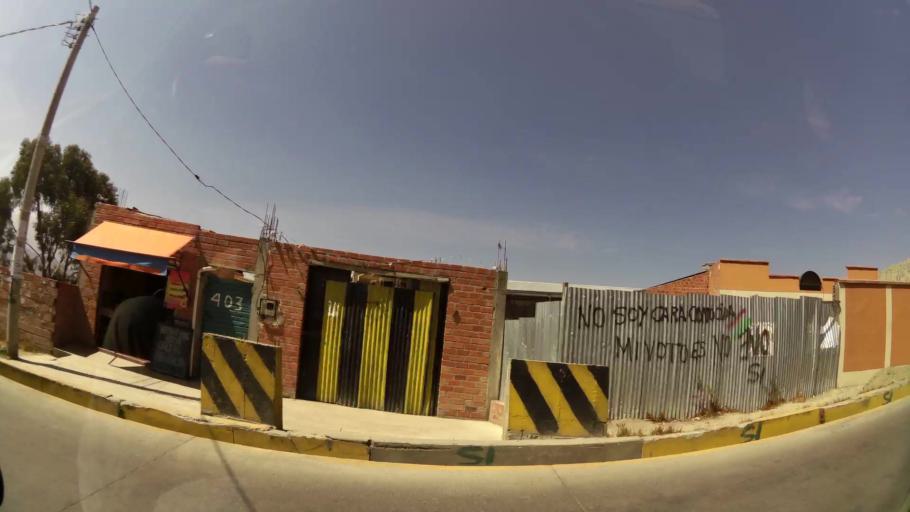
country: BO
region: La Paz
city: La Paz
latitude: -16.5313
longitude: -68.1293
